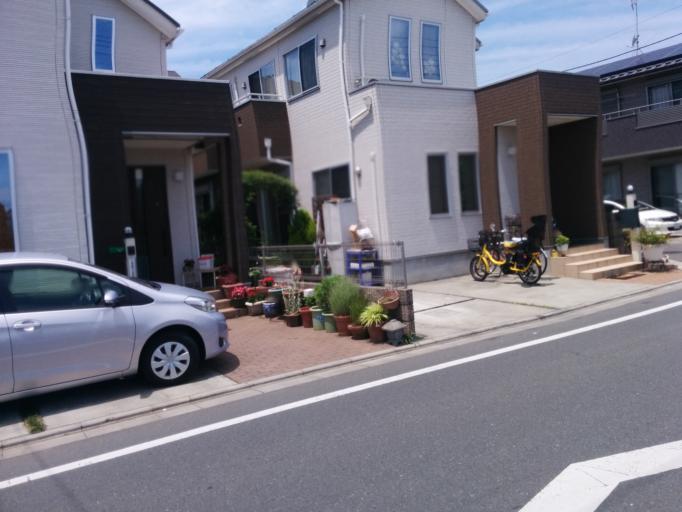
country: JP
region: Tokyo
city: Higashimurayama-shi
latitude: 35.7623
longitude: 139.4777
